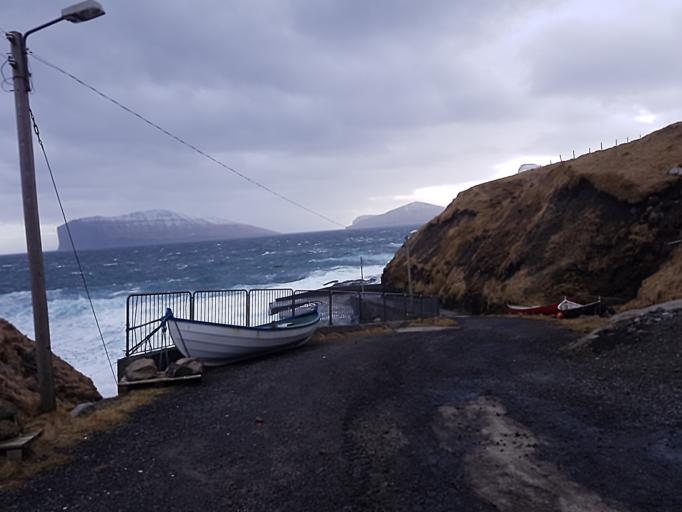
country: FO
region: Nordoyar
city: Klaksvik
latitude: 62.3549
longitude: -6.5192
